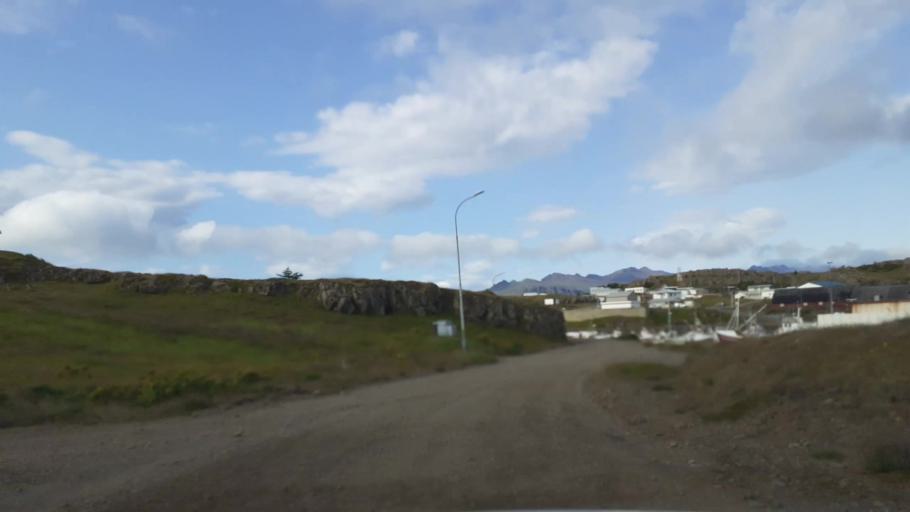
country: IS
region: East
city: Reydarfjoerdur
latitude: 64.6578
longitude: -14.2773
